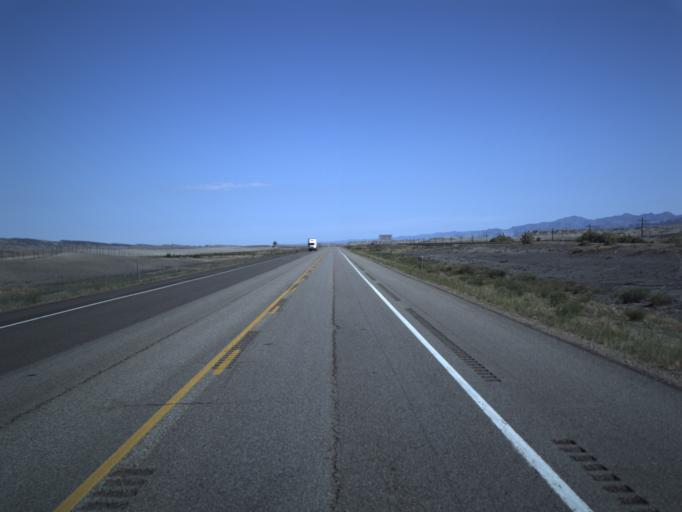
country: US
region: Utah
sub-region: Carbon County
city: East Carbon City
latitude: 39.1062
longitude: -110.3254
